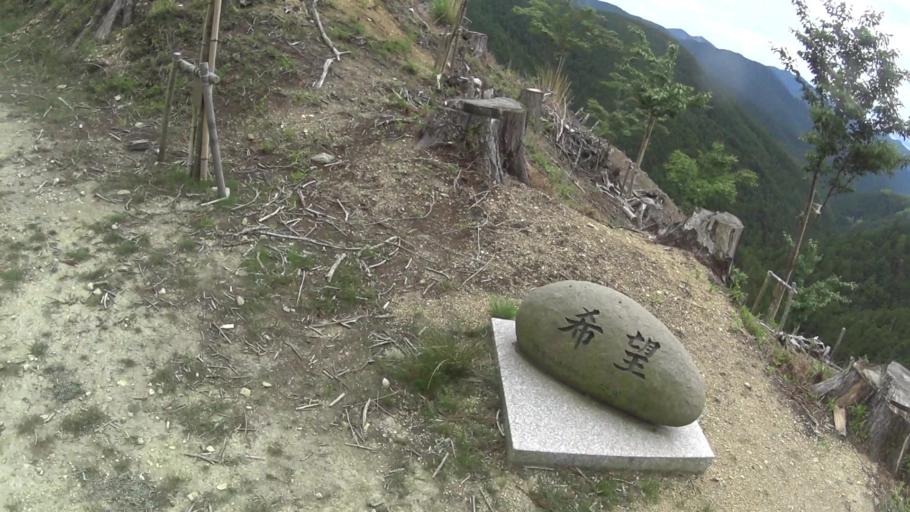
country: JP
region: Nara
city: Yoshino-cho
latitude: 34.3413
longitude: 135.8846
